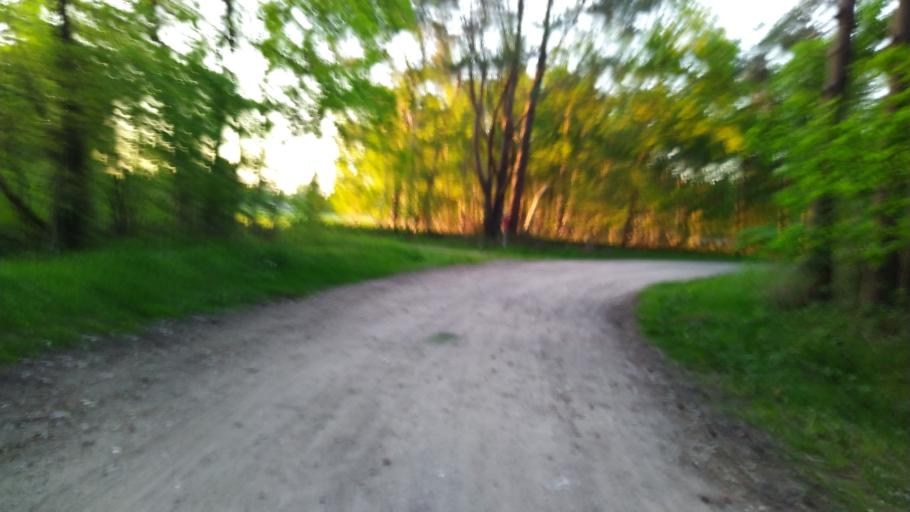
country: DE
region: Lower Saxony
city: Bargstedt
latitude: 53.4879
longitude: 9.4396
